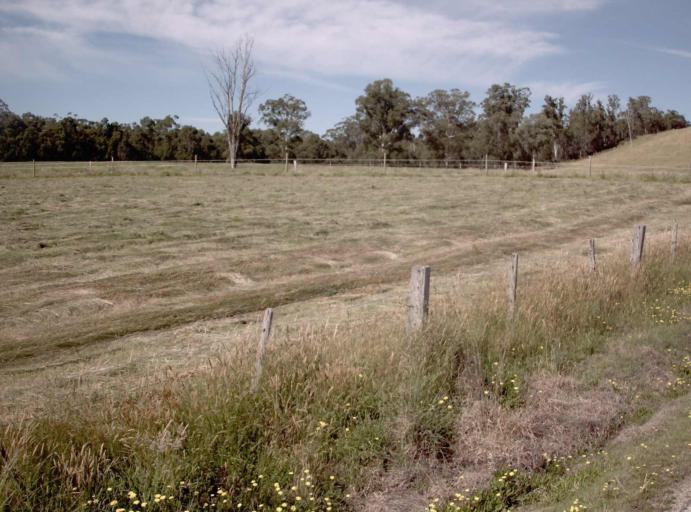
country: AU
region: Victoria
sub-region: East Gippsland
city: Lakes Entrance
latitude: -37.5239
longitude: 148.1452
